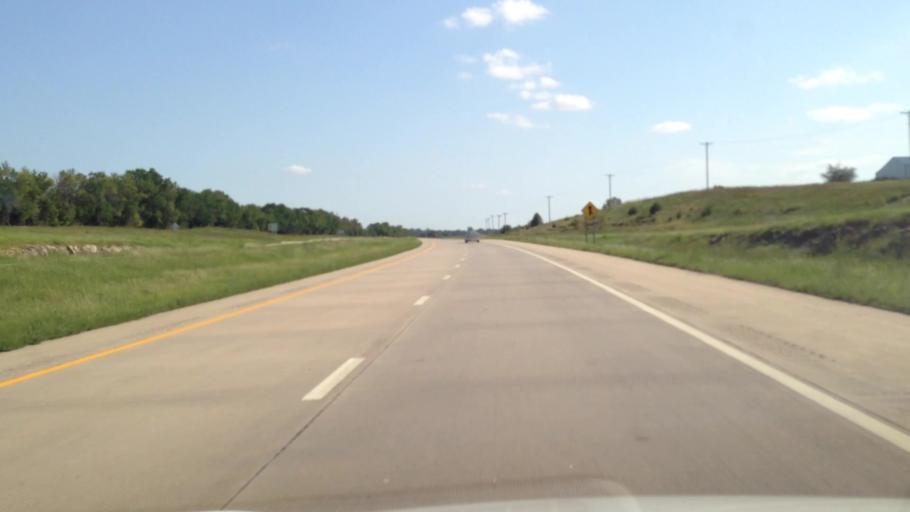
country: US
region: Kansas
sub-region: Bourbon County
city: Fort Scott
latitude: 37.8917
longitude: -94.7056
